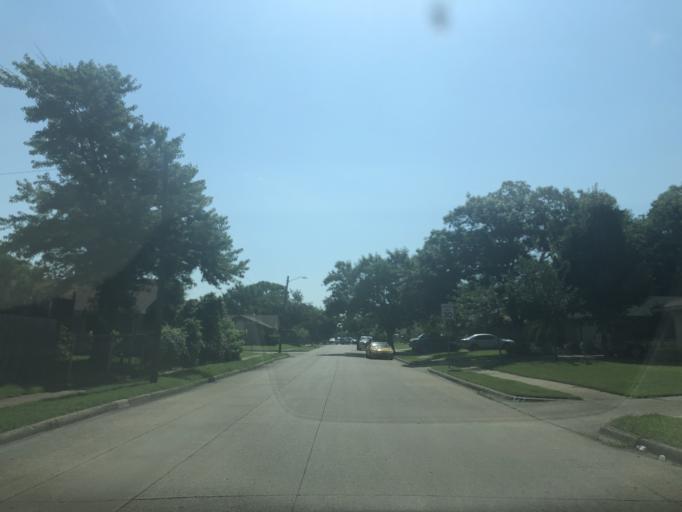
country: US
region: Texas
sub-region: Dallas County
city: Grand Prairie
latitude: 32.7225
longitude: -97.0003
